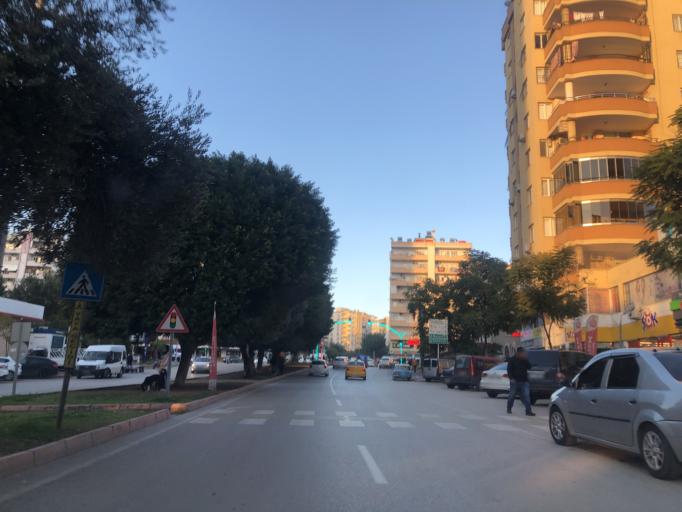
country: TR
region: Adana
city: Adana
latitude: 37.0285
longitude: 35.2989
